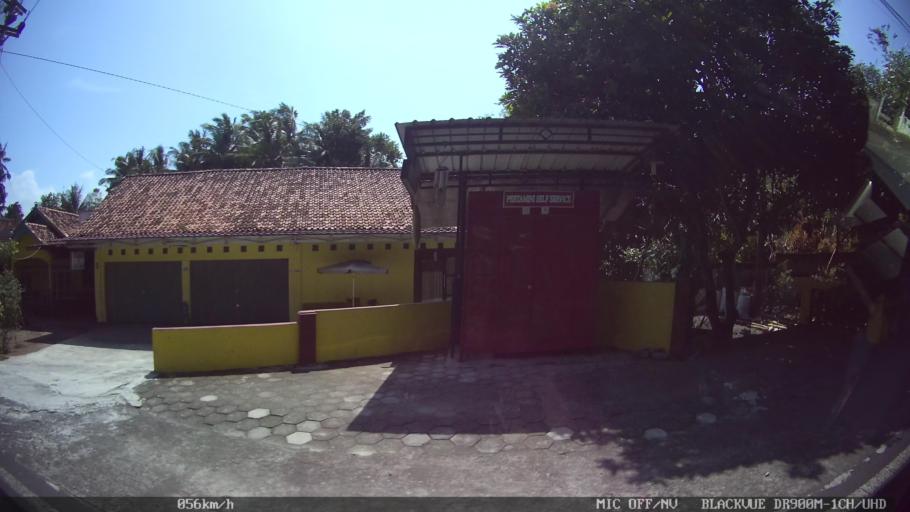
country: ID
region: Daerah Istimewa Yogyakarta
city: Srandakan
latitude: -7.9019
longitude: 110.0719
